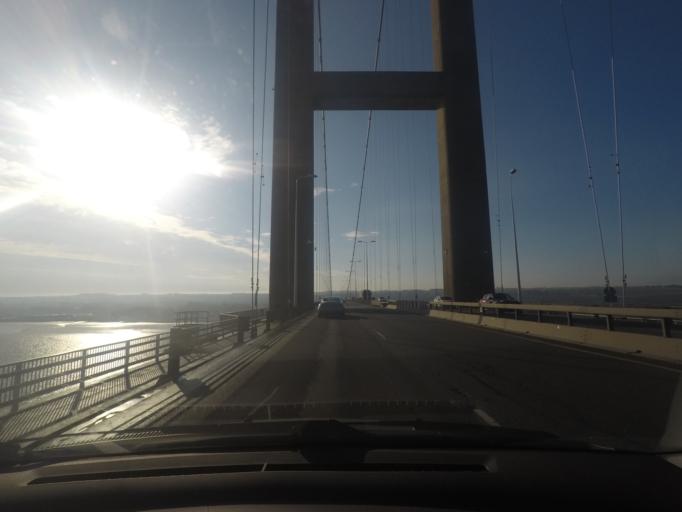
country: GB
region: England
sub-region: East Riding of Yorkshire
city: Hessle
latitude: 53.7023
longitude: -0.4493
